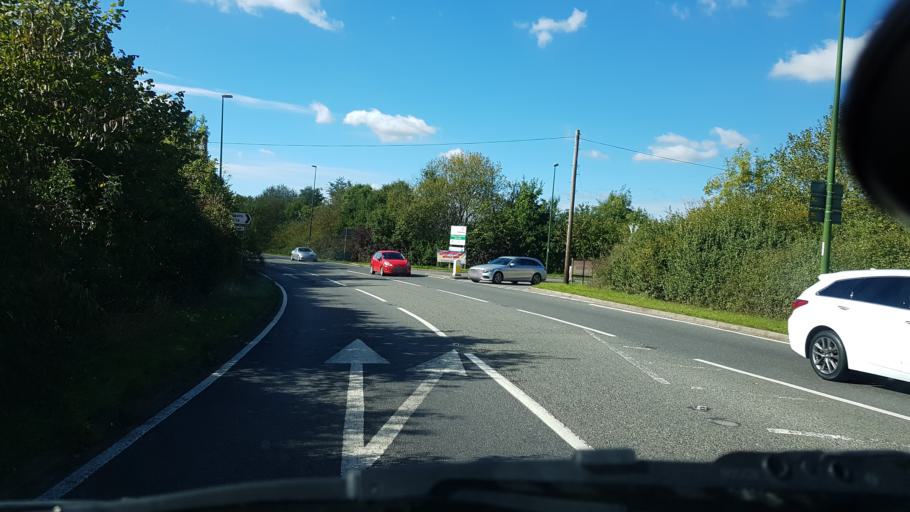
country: GB
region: England
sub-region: West Sussex
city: Billingshurst
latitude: 51.0229
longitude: -0.4615
